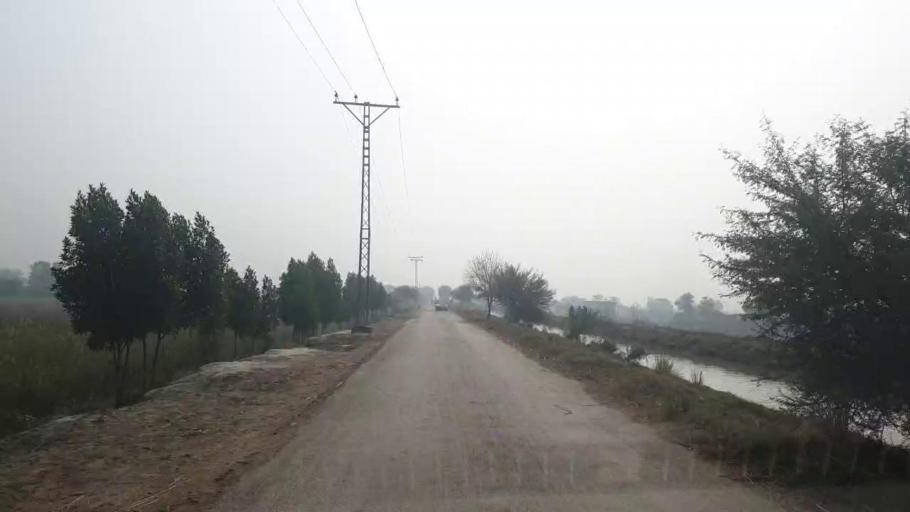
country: PK
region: Sindh
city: Tando Adam
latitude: 25.7595
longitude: 68.6127
